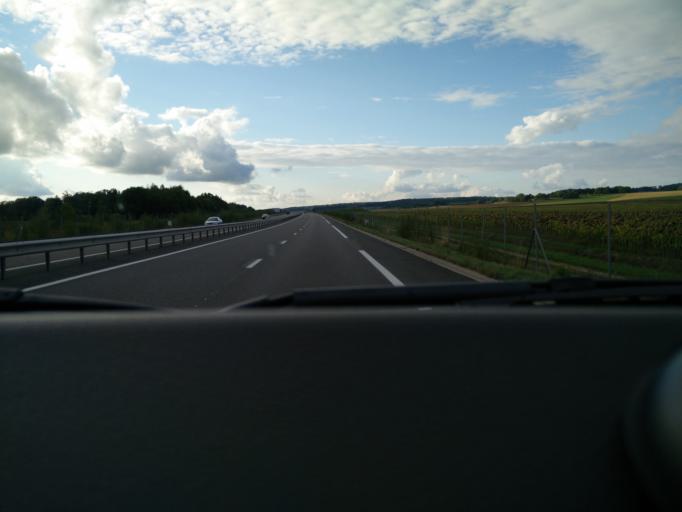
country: FR
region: Lorraine
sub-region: Departement de Meurthe-et-Moselle
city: Baccarat
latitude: 48.4729
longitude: 6.7244
